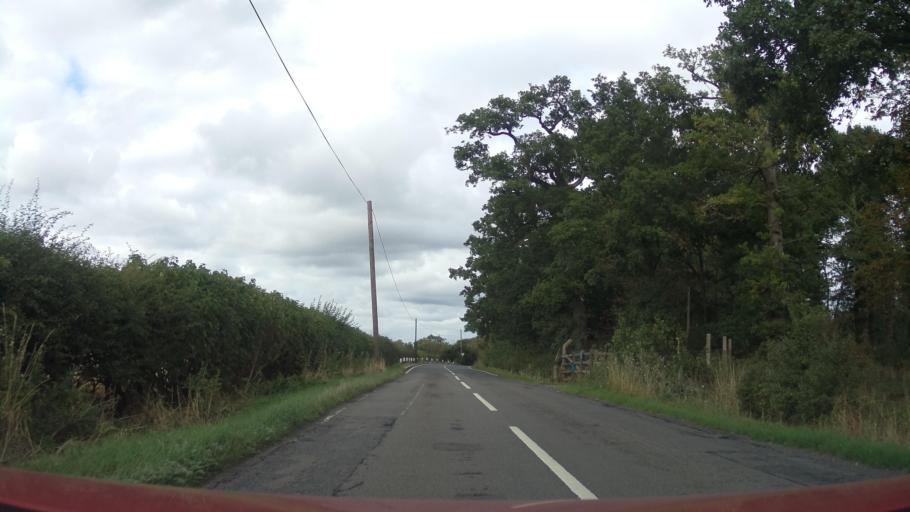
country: GB
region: England
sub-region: Nottinghamshire
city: East Leake
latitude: 52.8120
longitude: -1.1841
